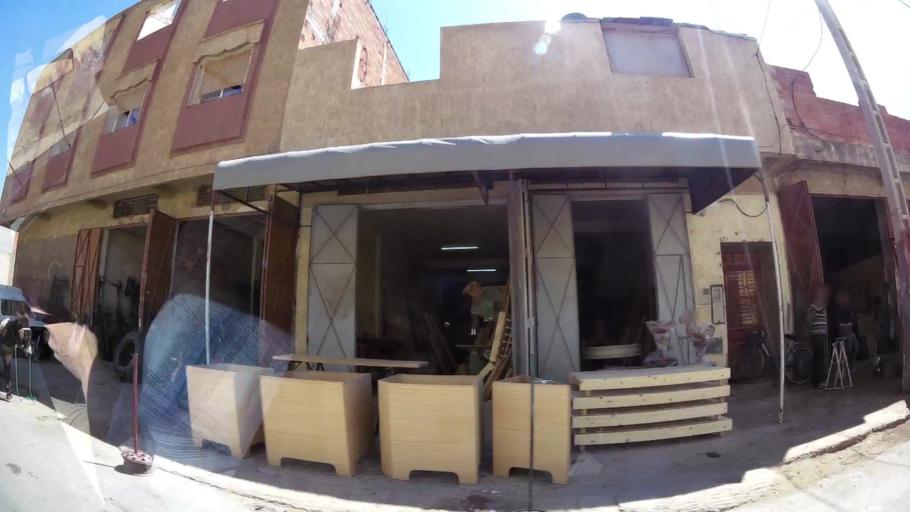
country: MA
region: Oriental
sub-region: Oujda-Angad
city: Oujda
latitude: 34.6884
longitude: -1.9371
